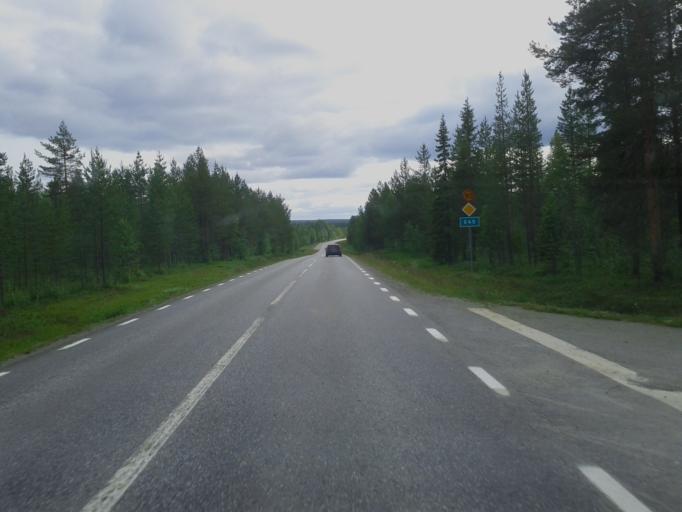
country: SE
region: Vaesterbotten
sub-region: Sorsele Kommun
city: Sorsele
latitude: 65.2264
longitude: 17.6500
